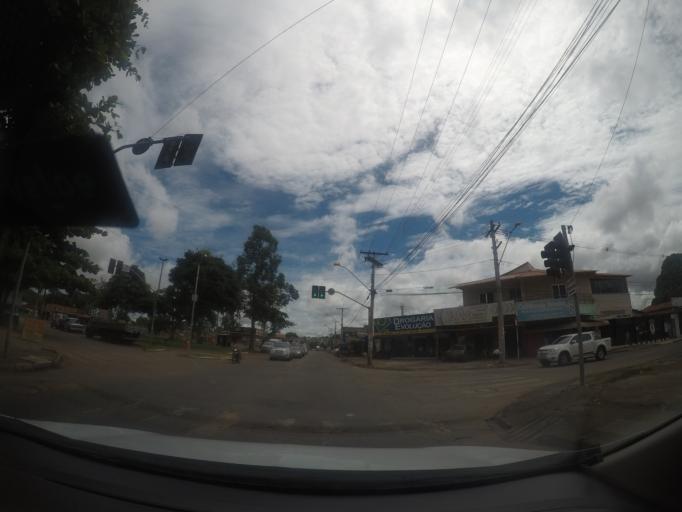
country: BR
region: Goias
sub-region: Goiania
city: Goiania
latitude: -16.6603
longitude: -49.3019
